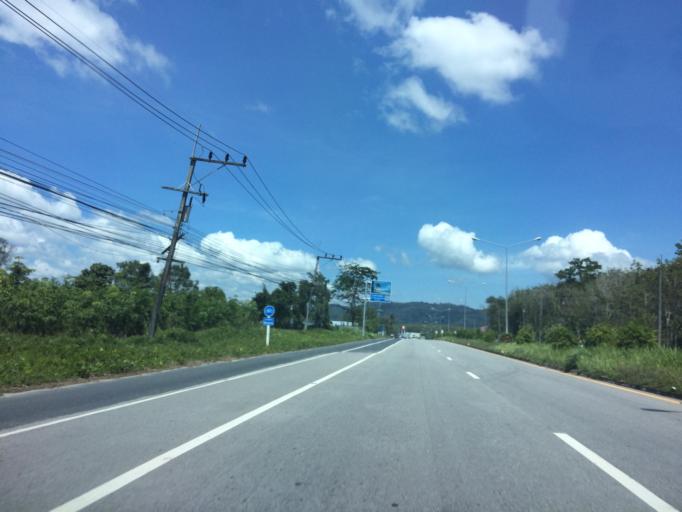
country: TH
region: Phangnga
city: Thai Mueang
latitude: 8.2501
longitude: 98.2984
